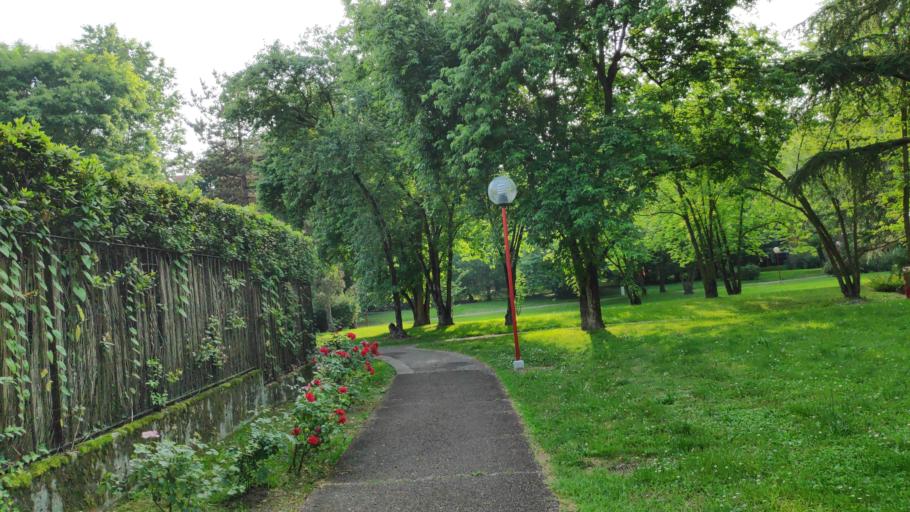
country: IT
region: Lombardy
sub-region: Citta metropolitana di Milano
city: Basiglio
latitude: 45.3618
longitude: 9.1657
